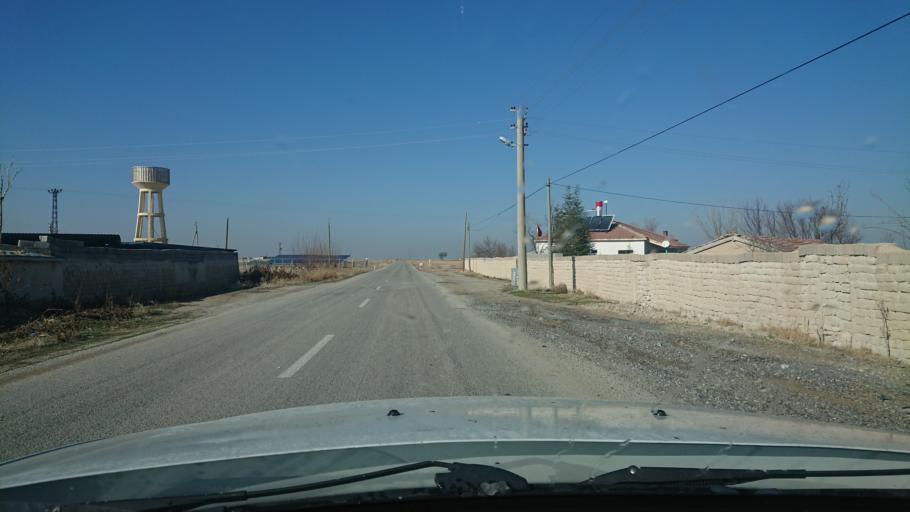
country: TR
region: Aksaray
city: Sultanhani
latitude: 38.2940
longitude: 33.5165
